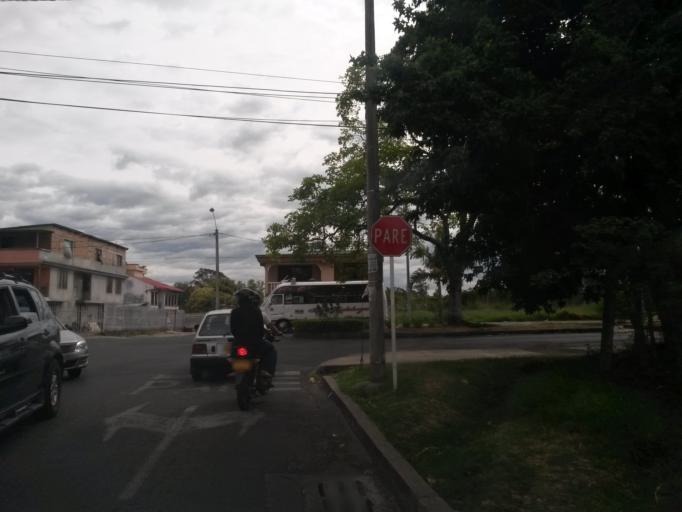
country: CO
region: Cauca
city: Popayan
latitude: 2.4514
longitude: -76.6095
